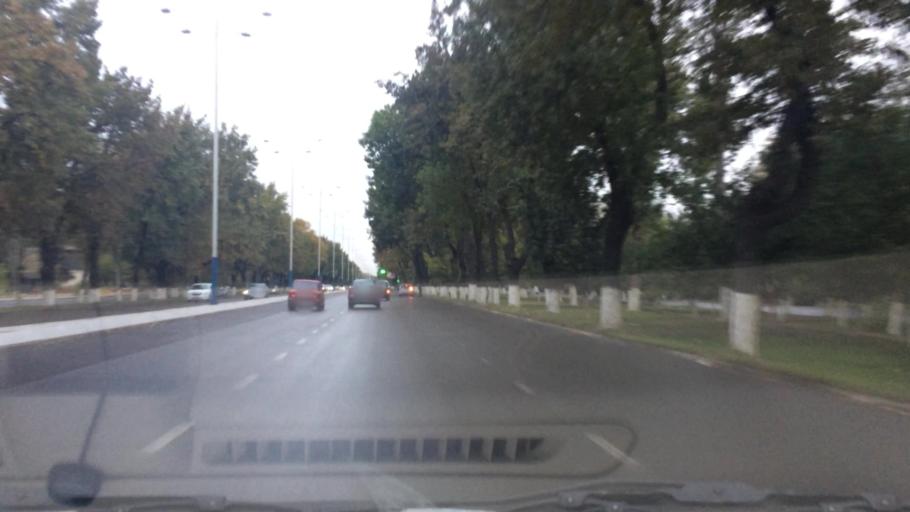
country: UZ
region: Toshkent Shahri
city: Tashkent
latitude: 41.2669
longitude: 69.2000
